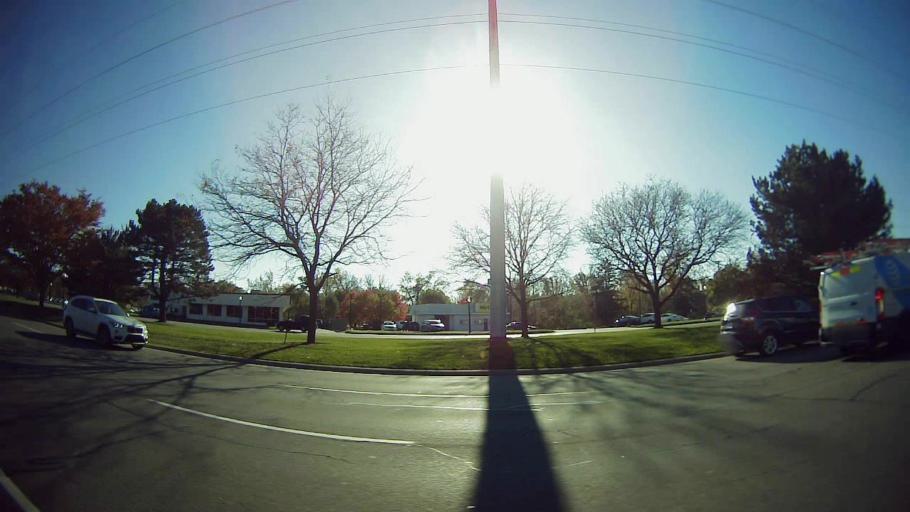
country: US
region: Michigan
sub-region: Oakland County
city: Farmington
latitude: 42.4481
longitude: -83.3357
